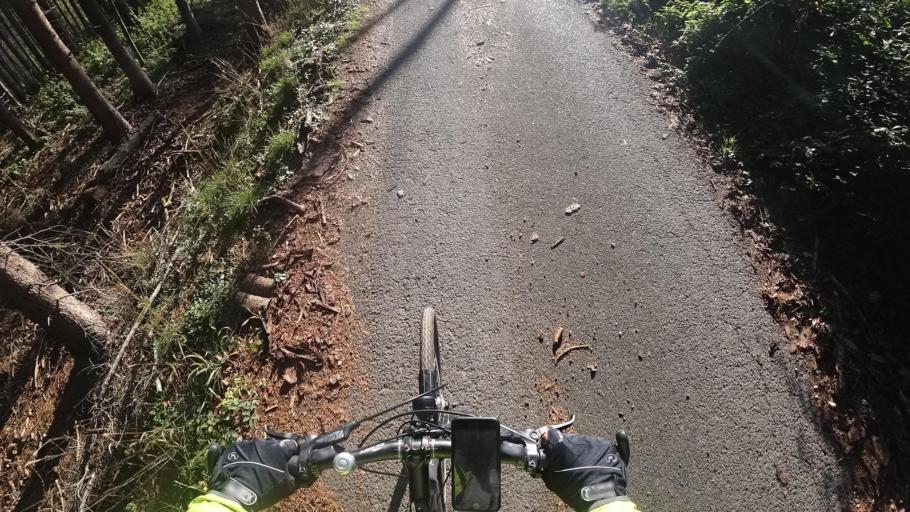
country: DE
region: Rheinland-Pfalz
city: Lind
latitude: 50.5039
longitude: 6.9145
